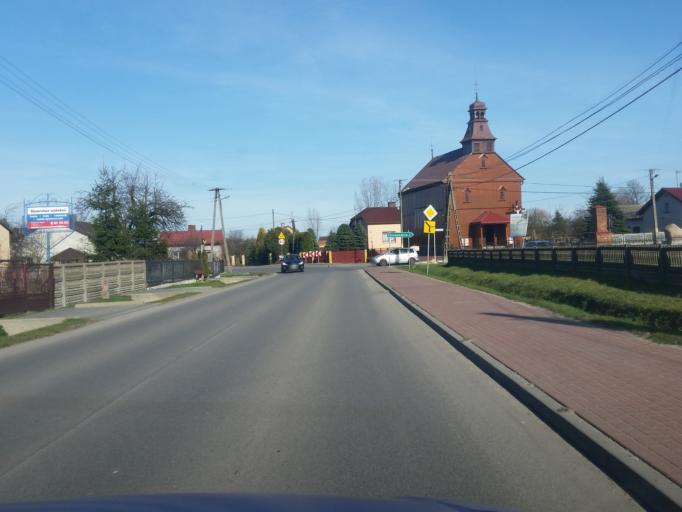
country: PL
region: Lodz Voivodeship
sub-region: Powiat radomszczanski
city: Kamiensk
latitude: 51.2090
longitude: 19.5451
